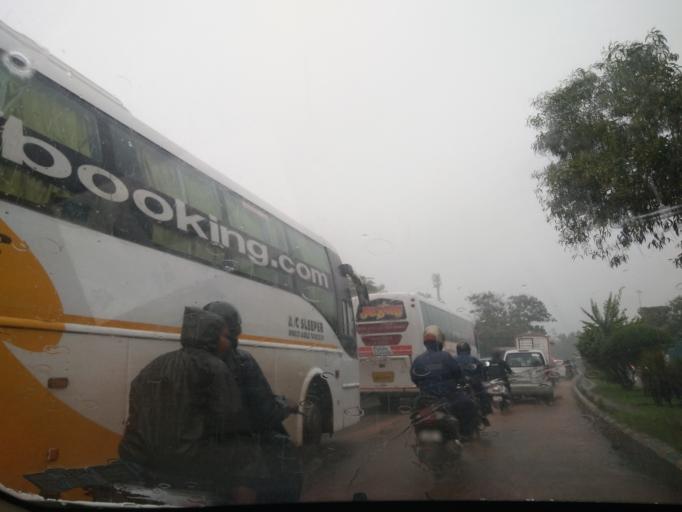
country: IN
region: Goa
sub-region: North Goa
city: Panaji
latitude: 15.4945
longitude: 73.8392
